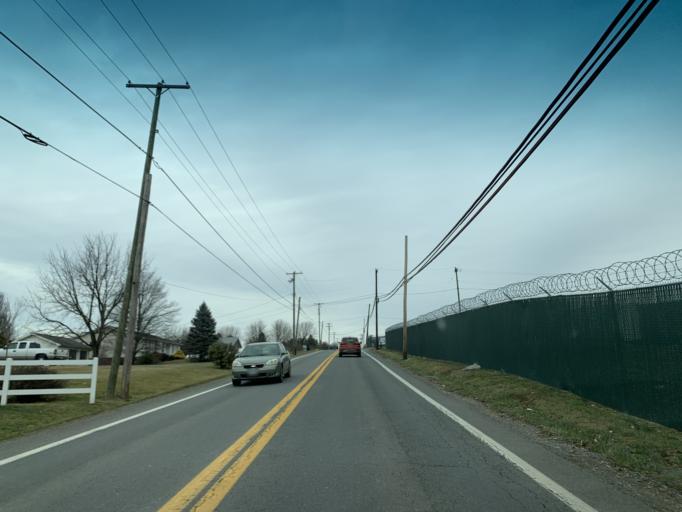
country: US
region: West Virginia
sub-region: Berkeley County
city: Martinsburg
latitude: 39.5308
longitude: -77.9155
